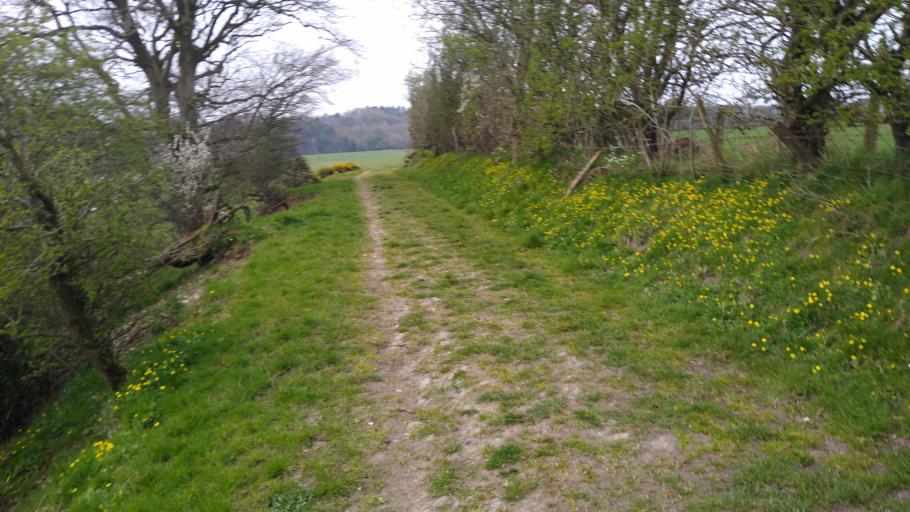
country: GB
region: England
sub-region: Cumbria
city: Dearham
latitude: 54.6601
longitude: -3.4471
